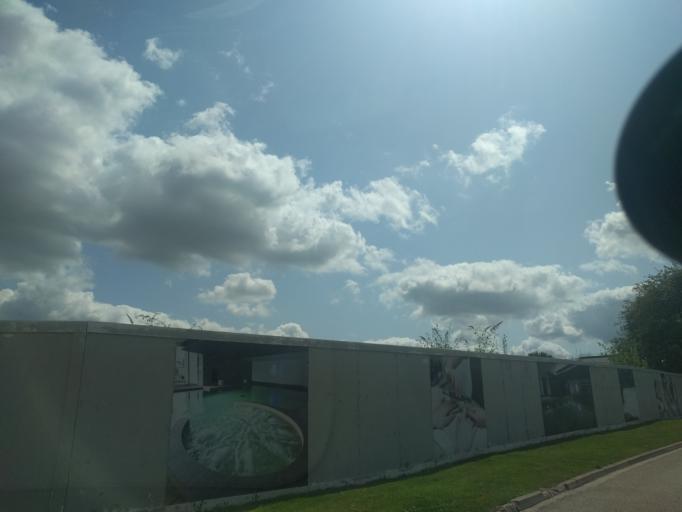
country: GB
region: England
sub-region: Wiltshire
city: Neston
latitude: 51.4148
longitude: -2.2154
